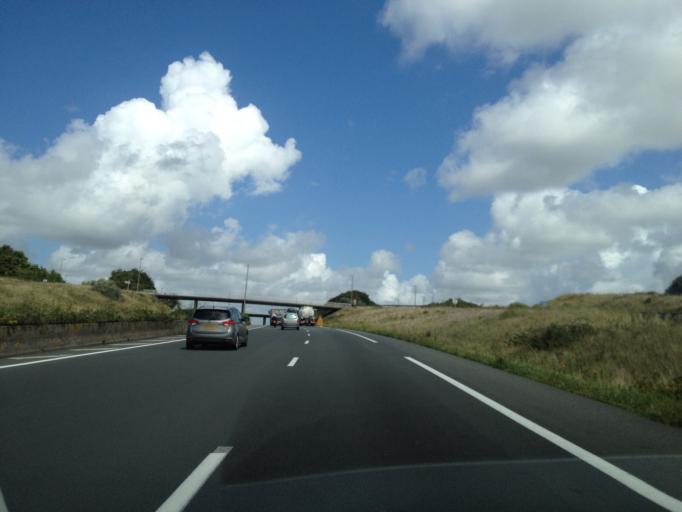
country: FR
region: Nord-Pas-de-Calais
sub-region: Departement du Pas-de-Calais
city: Wimille
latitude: 50.7694
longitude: 1.6474
